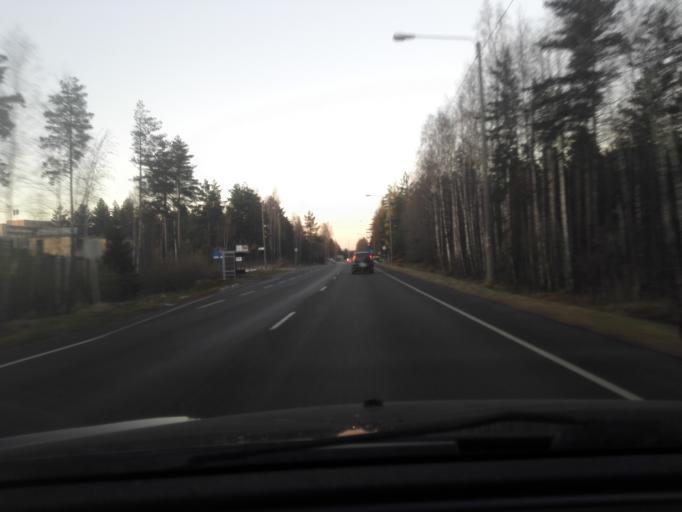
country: FI
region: Uusimaa
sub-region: Helsinki
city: Vantaa
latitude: 60.3015
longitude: 25.1038
